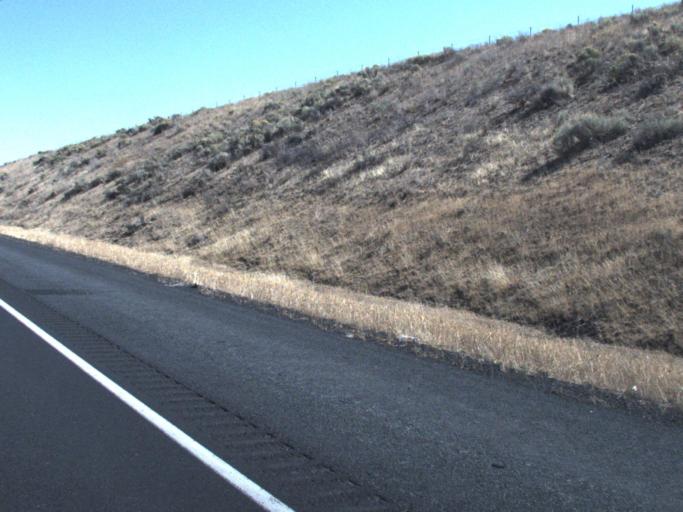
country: US
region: Washington
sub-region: Grant County
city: Warden
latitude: 47.0861
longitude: -118.7331
